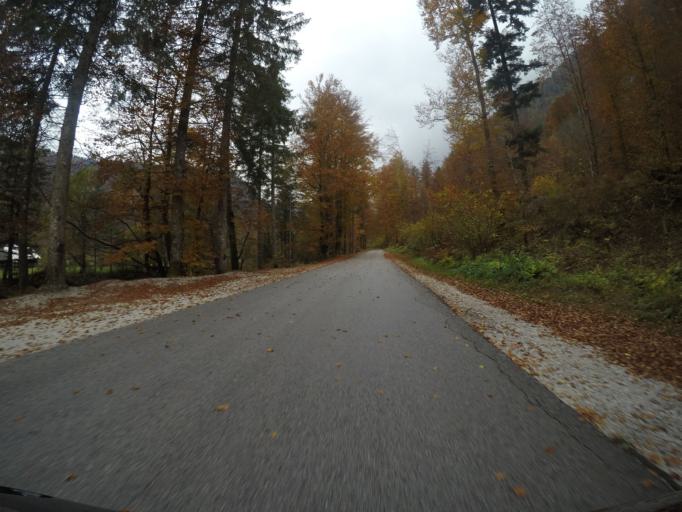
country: SI
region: Jesenice
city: Hrusica
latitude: 46.4165
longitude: 13.9900
